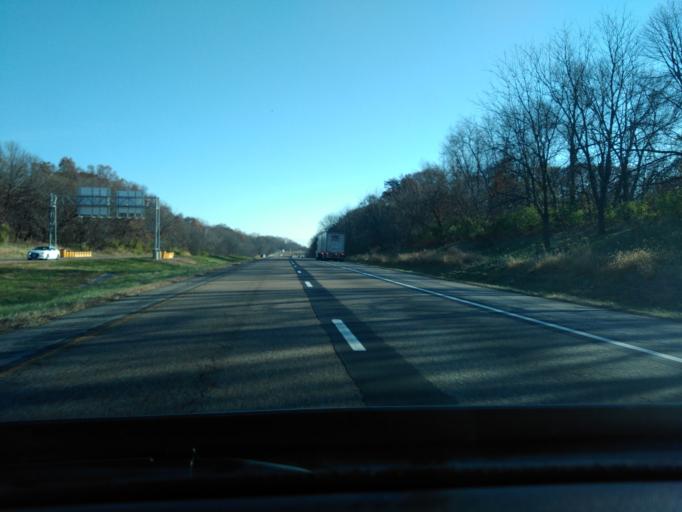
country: US
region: Illinois
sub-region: Madison County
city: Troy
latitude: 38.7540
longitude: -89.8888
